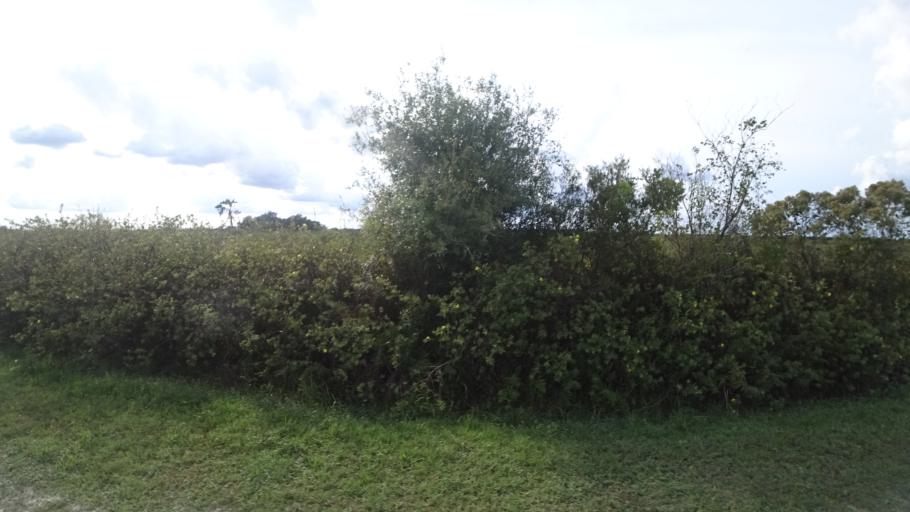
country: US
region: Florida
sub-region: DeSoto County
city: Nocatee
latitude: 27.2889
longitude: -82.1053
